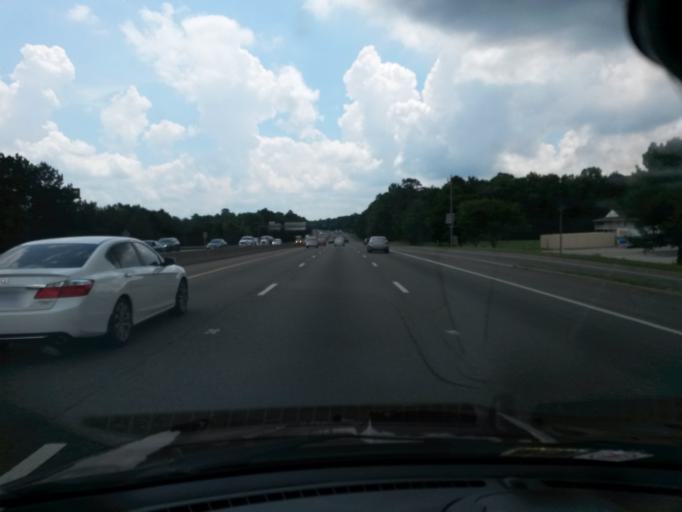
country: US
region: Virginia
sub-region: Chesterfield County
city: Bellwood
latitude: 37.4003
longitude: -77.4246
